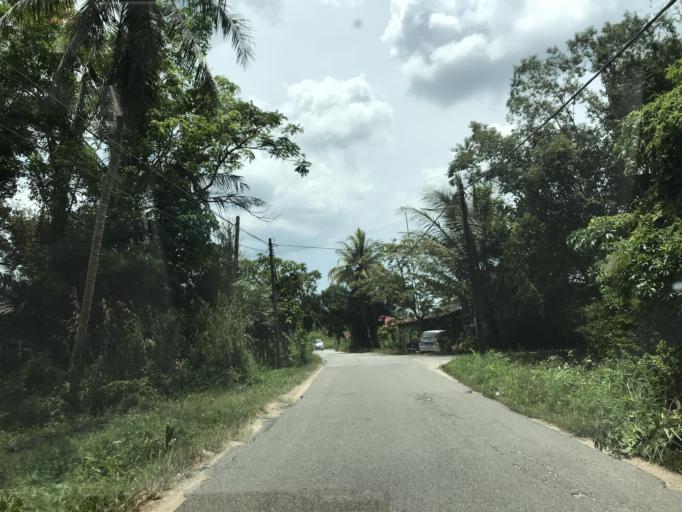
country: MY
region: Kelantan
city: Kota Bharu
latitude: 6.1367
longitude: 102.1839
